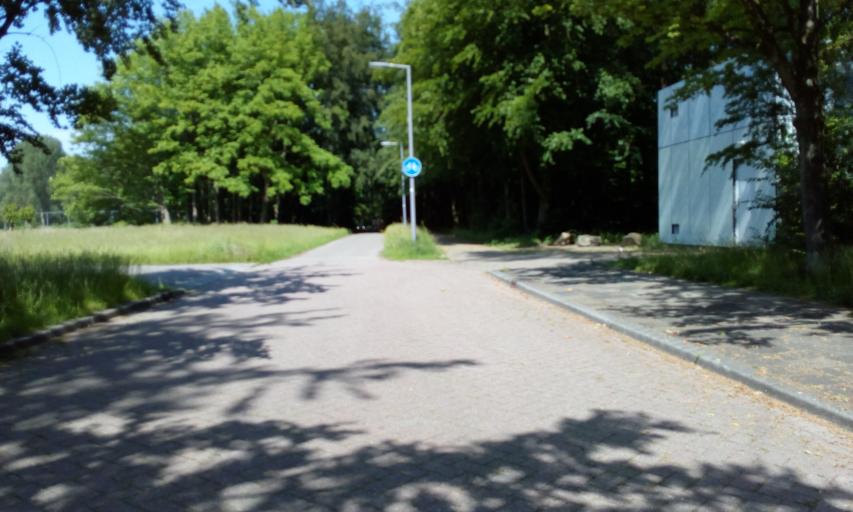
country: NL
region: South Holland
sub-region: Gemeente Rotterdam
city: Delfshaven
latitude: 51.8676
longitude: 4.4643
